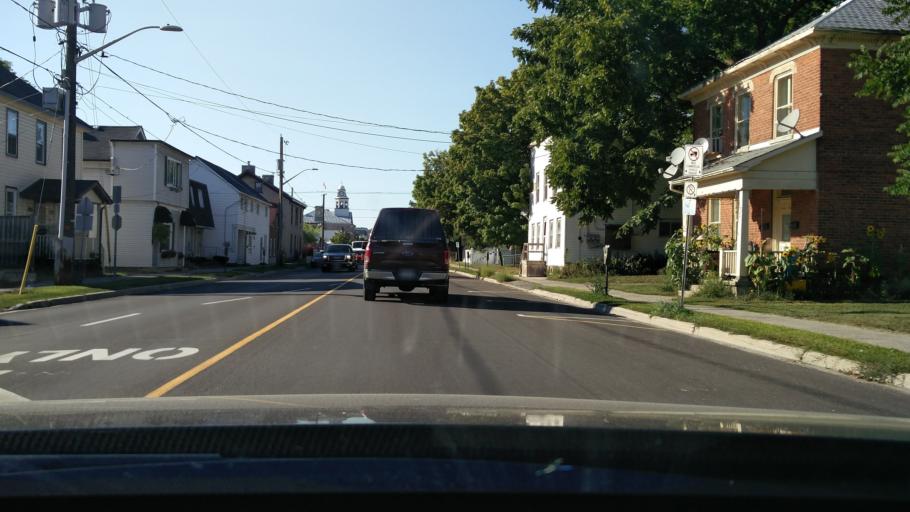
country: CA
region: Ontario
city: Perth
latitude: 44.8973
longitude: -76.2464
